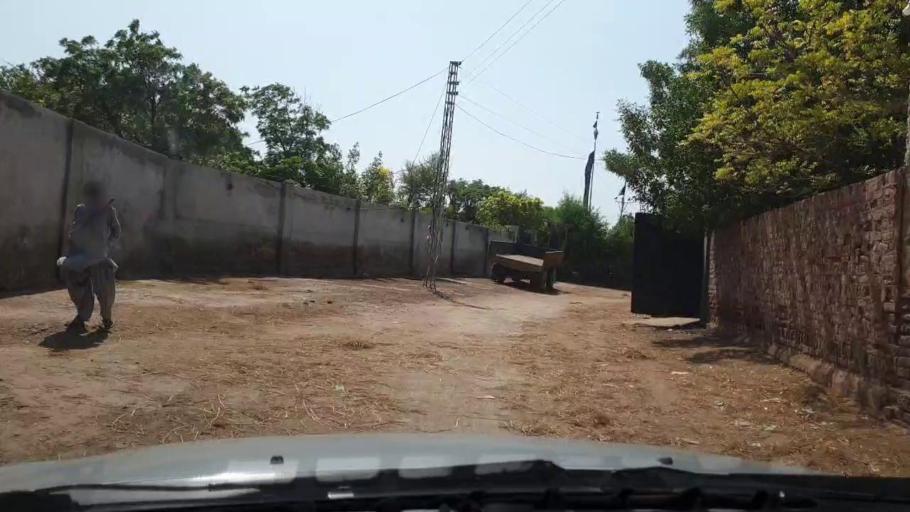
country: PK
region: Sindh
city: Tando Muhammad Khan
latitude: 25.1215
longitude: 68.6202
